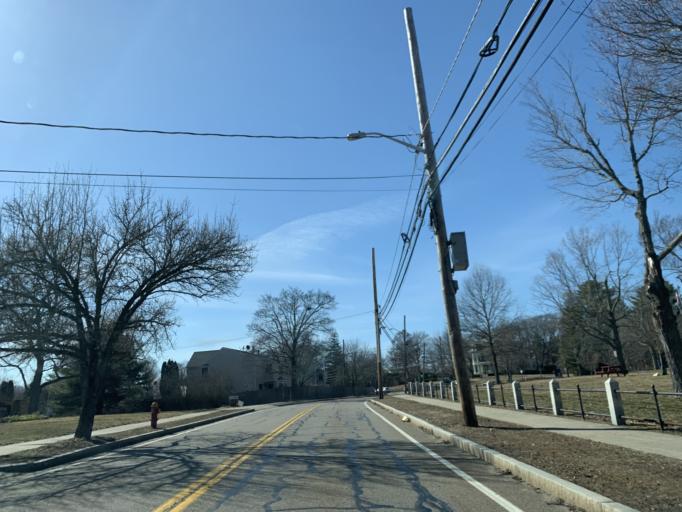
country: US
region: Massachusetts
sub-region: Norfolk County
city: Norwood
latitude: 42.1832
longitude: -71.2118
